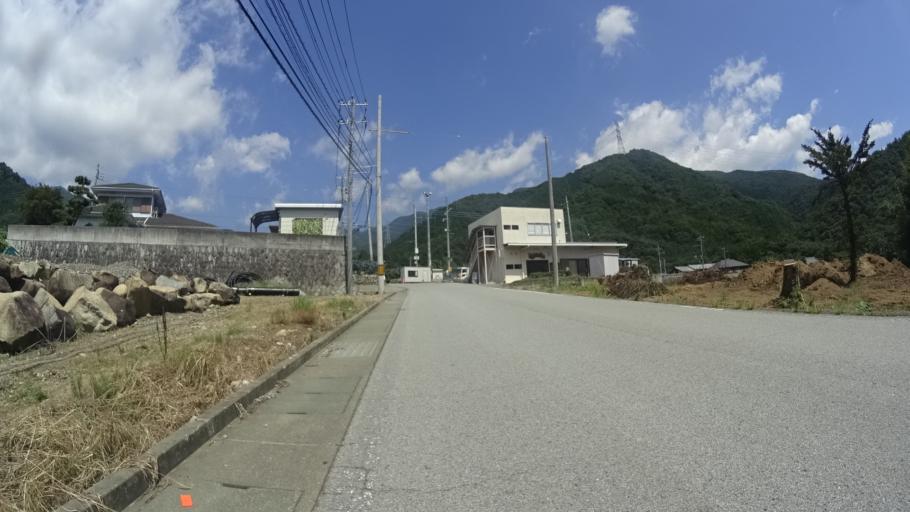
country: JP
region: Yamanashi
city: Enzan
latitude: 35.7679
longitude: 138.7037
